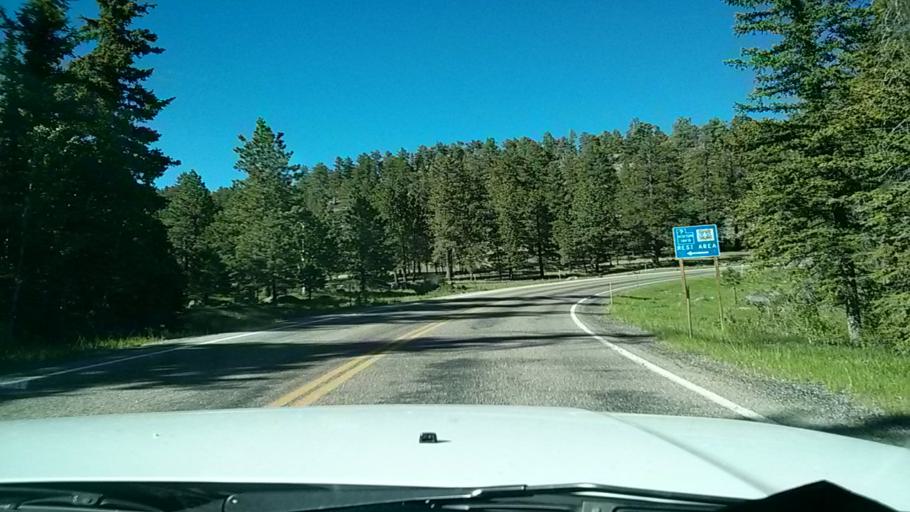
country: US
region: Utah
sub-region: Wayne County
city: Loa
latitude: 38.1089
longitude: -111.3348
